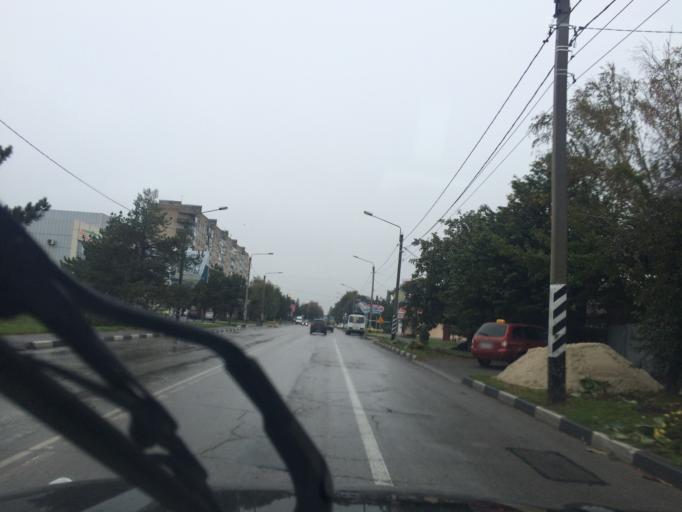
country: RU
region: Rostov
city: Azov
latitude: 47.0907
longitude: 39.4534
